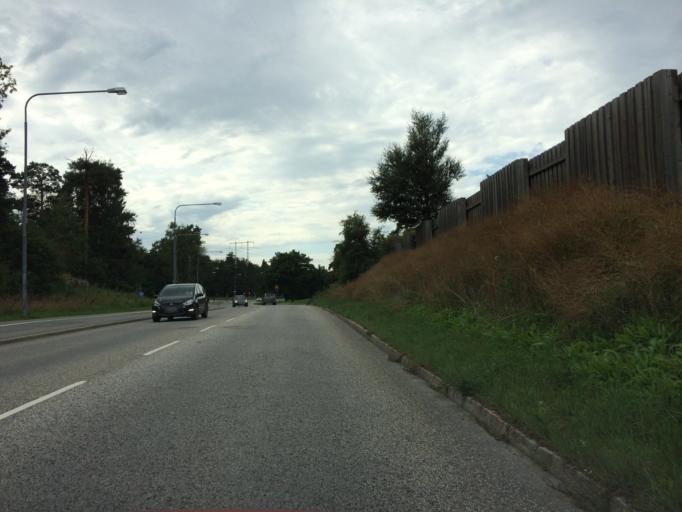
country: SE
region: Stockholm
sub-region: Huddinge Kommun
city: Huddinge
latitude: 59.2906
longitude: 17.9957
